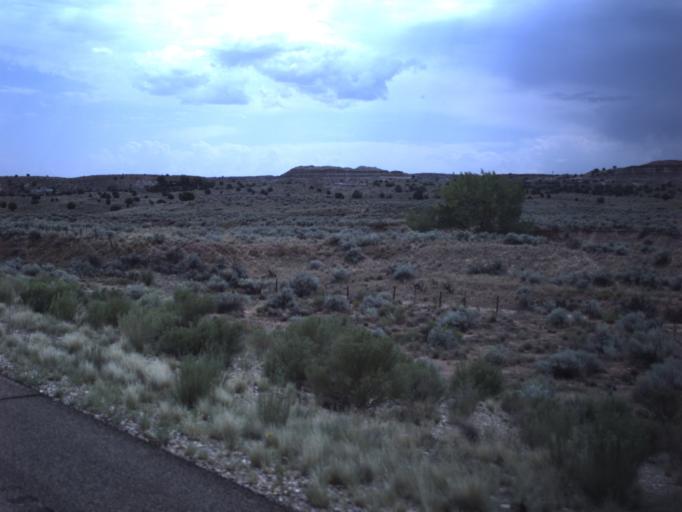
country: US
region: Arizona
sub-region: Coconino County
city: Page
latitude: 37.1161
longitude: -111.9369
